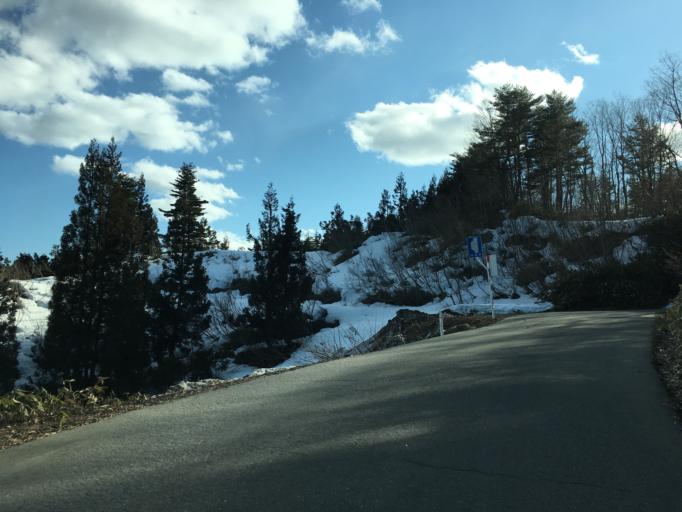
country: JP
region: Yamagata
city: Yonezawa
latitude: 37.9241
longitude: 139.9430
